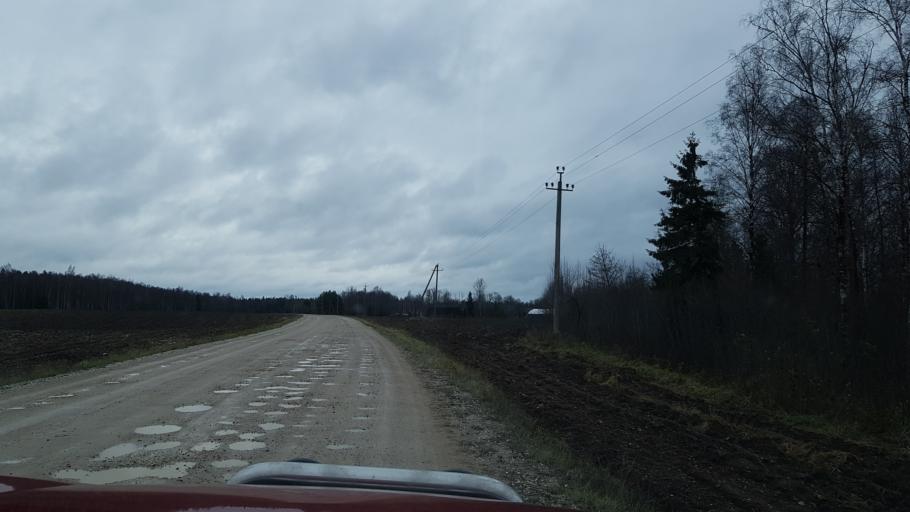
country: EE
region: Paernumaa
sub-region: Halinga vald
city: Parnu-Jaagupi
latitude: 58.5658
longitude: 24.4110
